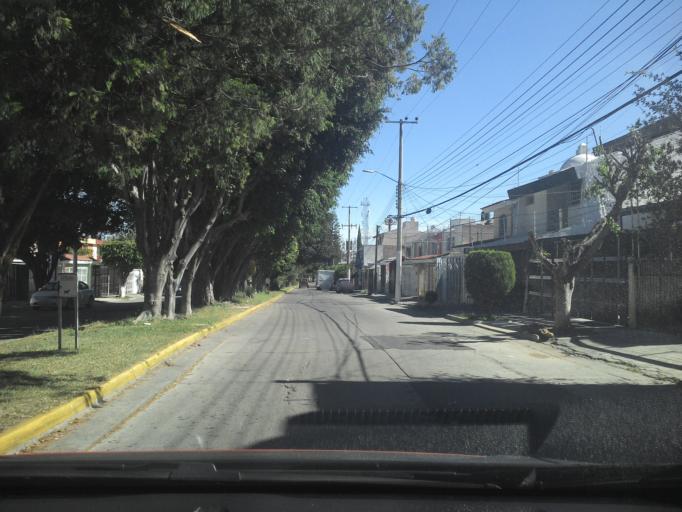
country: MX
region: Jalisco
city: Zapopan2
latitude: 20.7477
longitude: -103.4058
